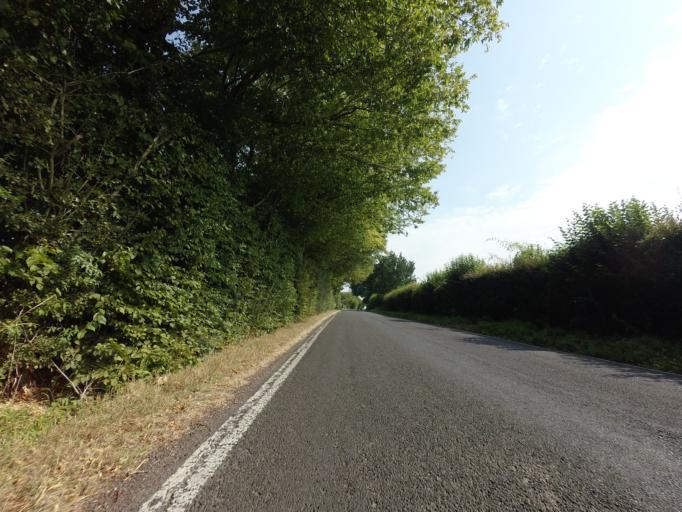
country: GB
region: England
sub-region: Kent
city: Staplehurst
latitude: 51.1352
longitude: 0.5828
